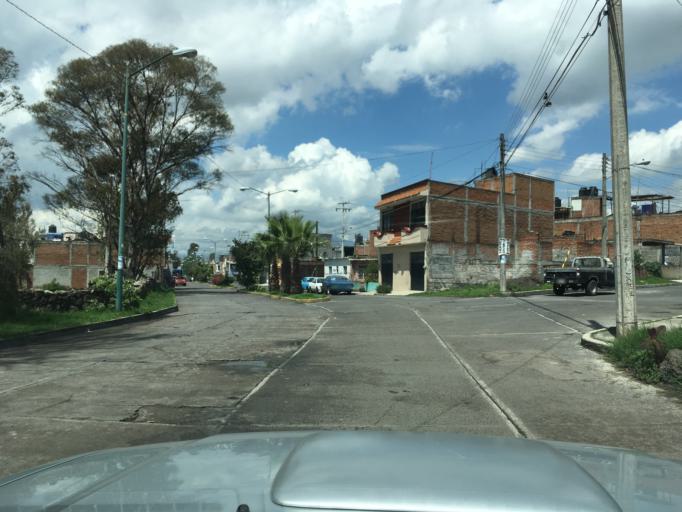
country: MX
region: Michoacan
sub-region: Tarimbaro
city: Real Hacienda (Metropolis)
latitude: 19.7284
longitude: -101.1998
